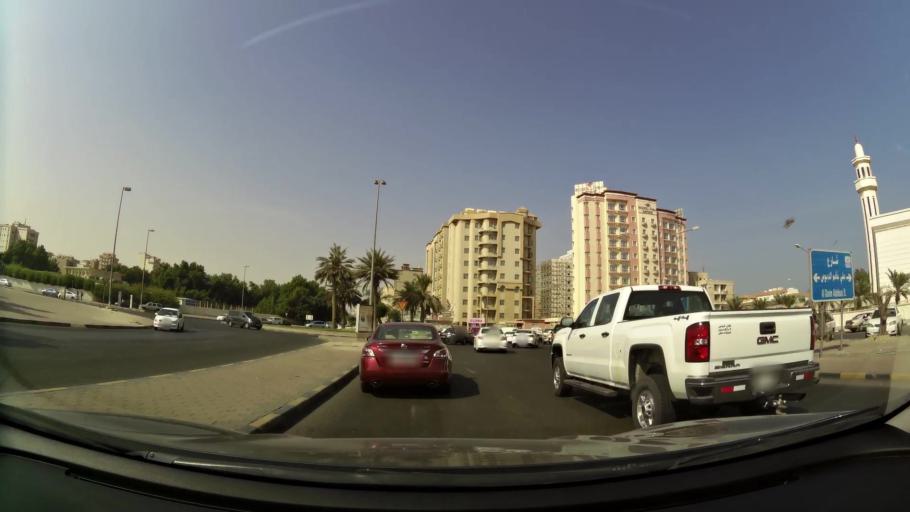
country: KW
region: Al Ahmadi
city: Al Fahahil
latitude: 29.0825
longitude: 48.1339
